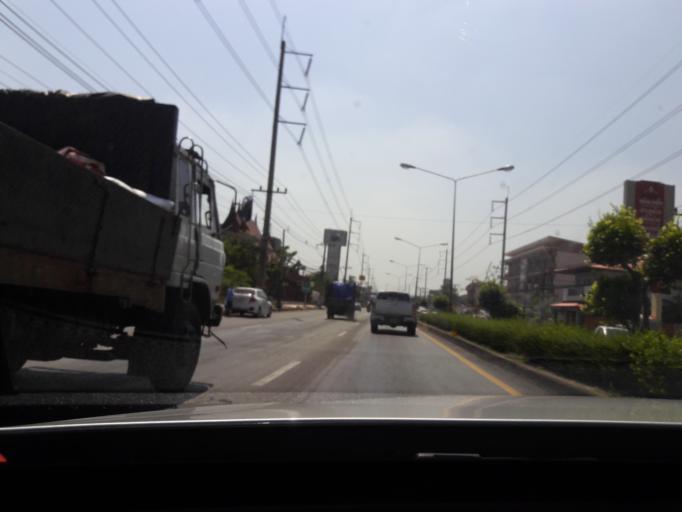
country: TH
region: Samut Sakhon
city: Krathum Baen
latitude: 13.6394
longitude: 100.2982
